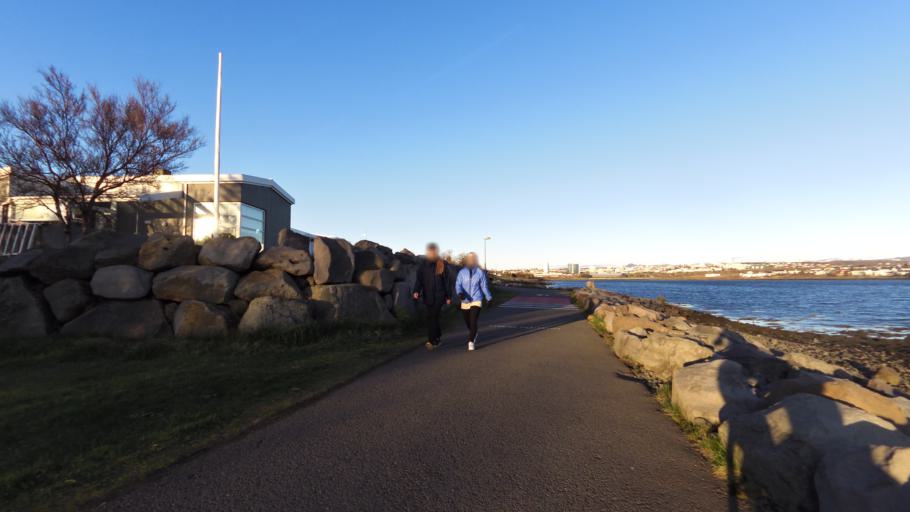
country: IS
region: Capital Region
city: Kopavogur
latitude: 64.1075
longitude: -21.9313
